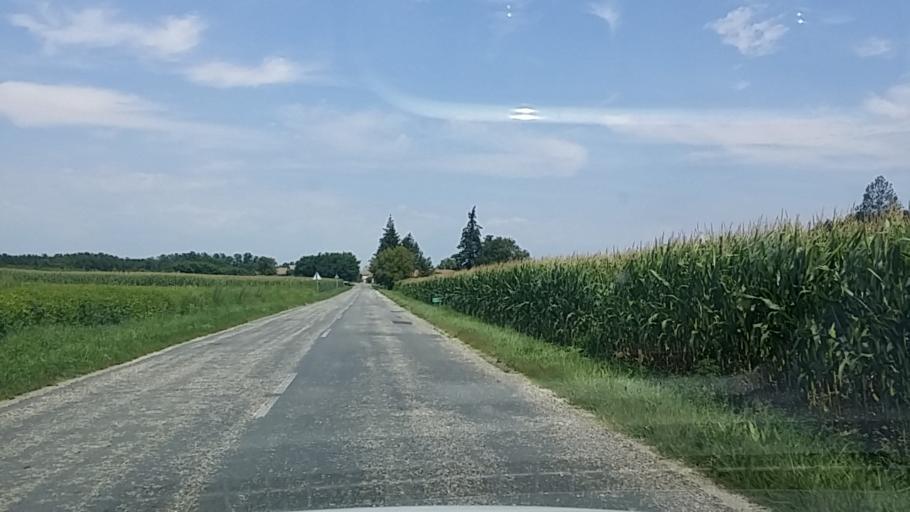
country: HU
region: Zala
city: Murakeresztur
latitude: 46.3690
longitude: 16.8968
